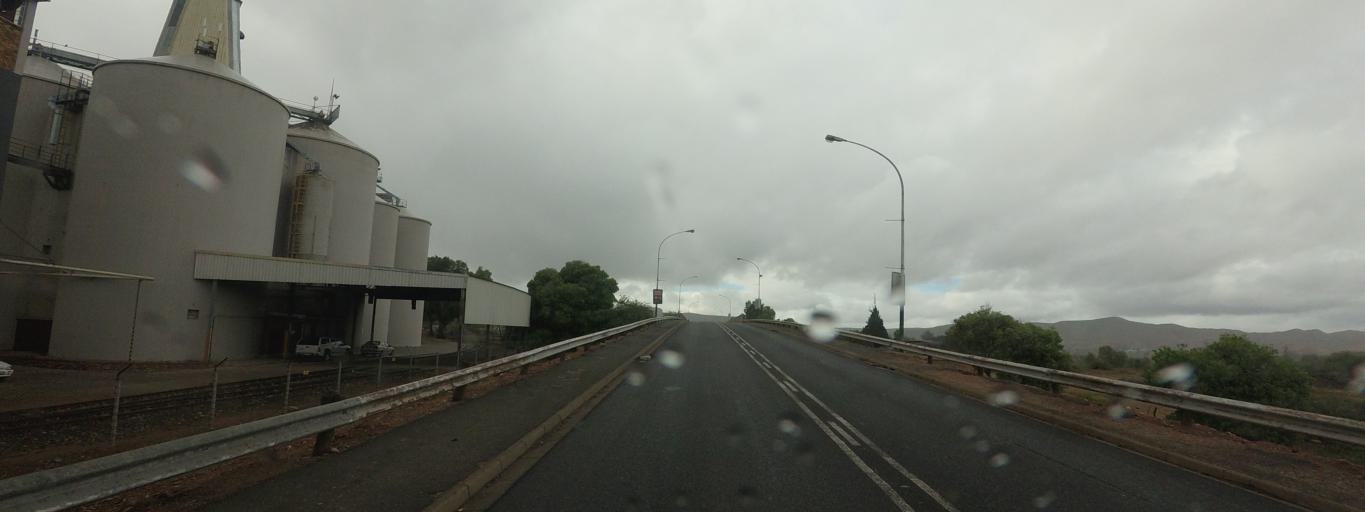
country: ZA
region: Western Cape
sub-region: Eden District Municipality
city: Oudtshoorn
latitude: -33.6096
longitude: 22.2130
